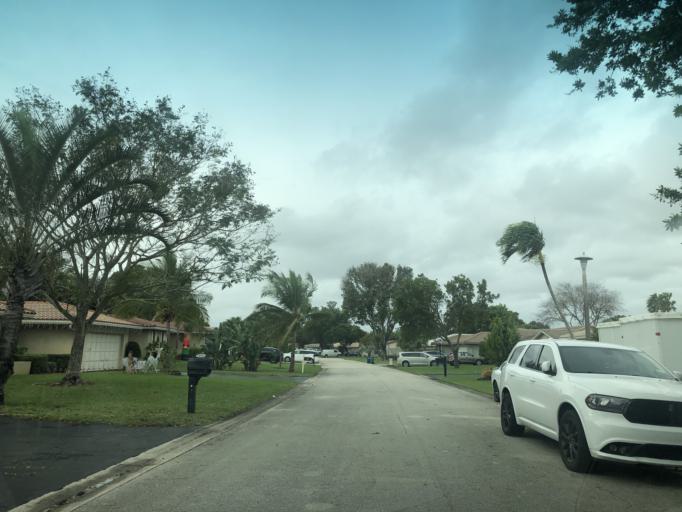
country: US
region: Florida
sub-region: Broward County
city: North Lauderdale
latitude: 26.2428
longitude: -80.2380
